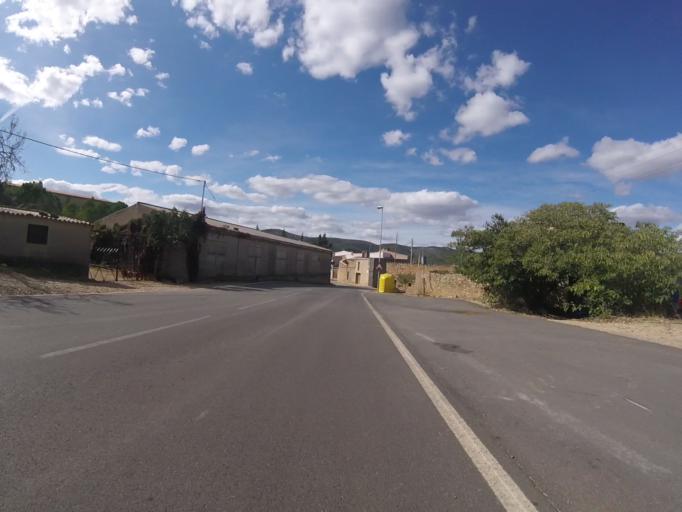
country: ES
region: Valencia
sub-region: Provincia de Castello
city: Cati
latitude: 40.4239
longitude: 0.0814
